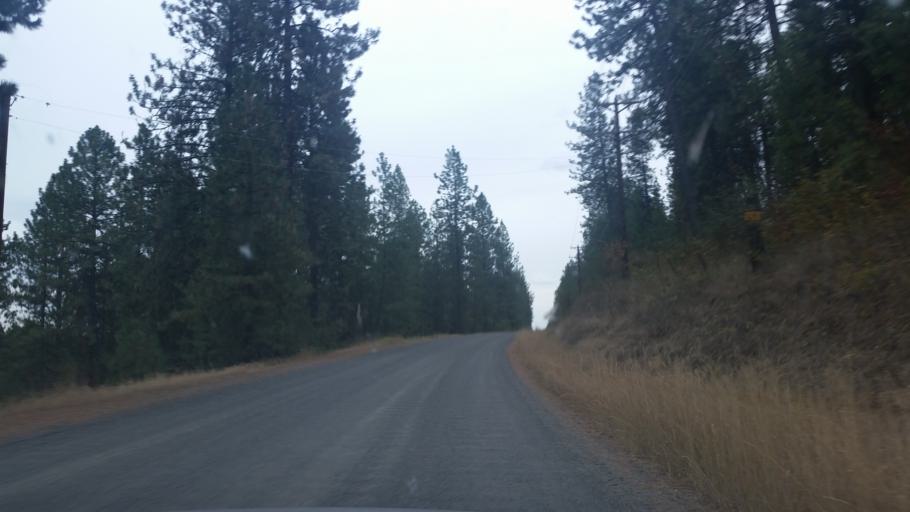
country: US
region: Washington
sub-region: Spokane County
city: Cheney
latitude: 47.5366
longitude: -117.5863
